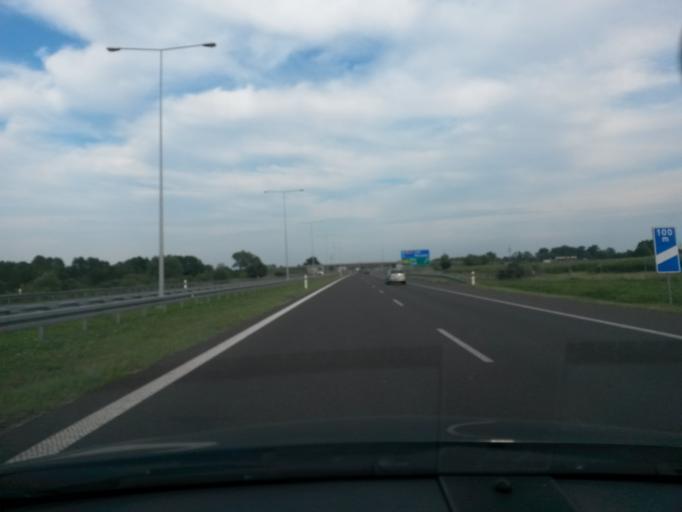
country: PL
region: Greater Poland Voivodeship
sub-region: Powiat turecki
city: Brudzew
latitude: 52.1415
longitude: 18.5994
